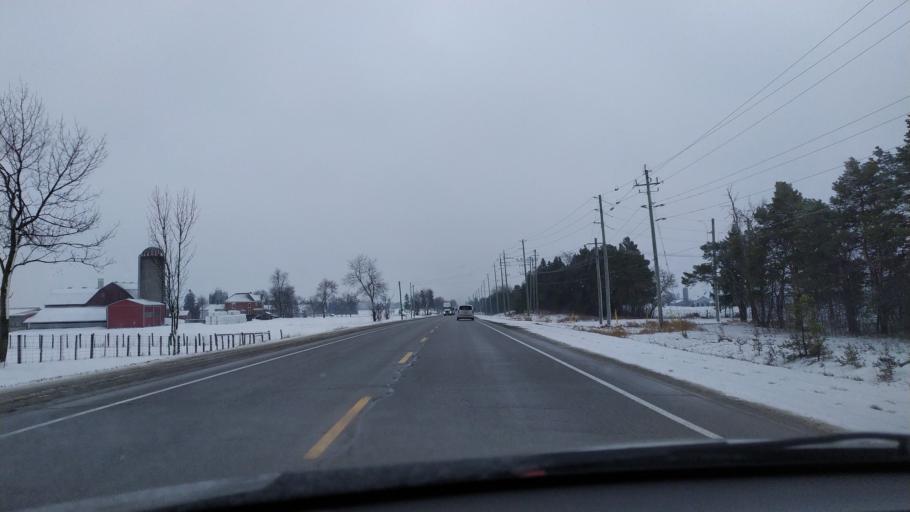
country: CA
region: Ontario
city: Waterloo
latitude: 43.6188
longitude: -80.6824
